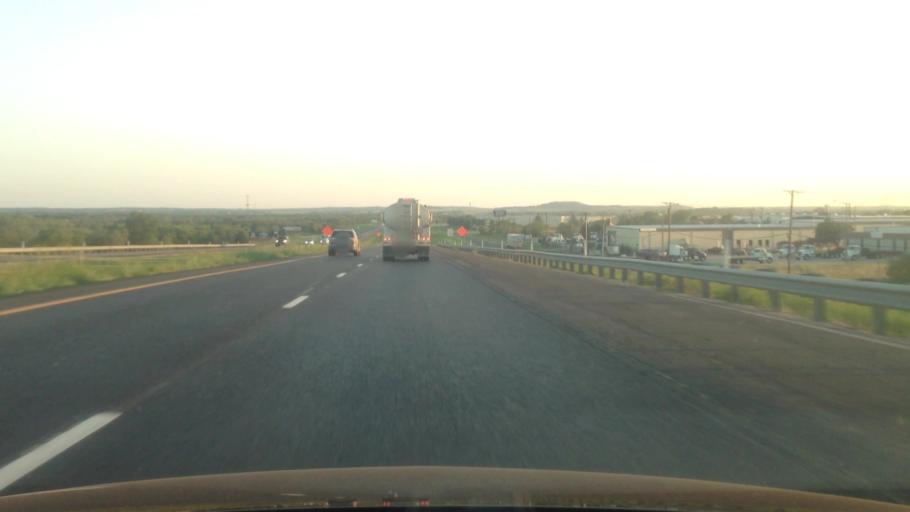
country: US
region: Texas
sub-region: Denton County
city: Denton
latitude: 33.2006
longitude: -97.1654
